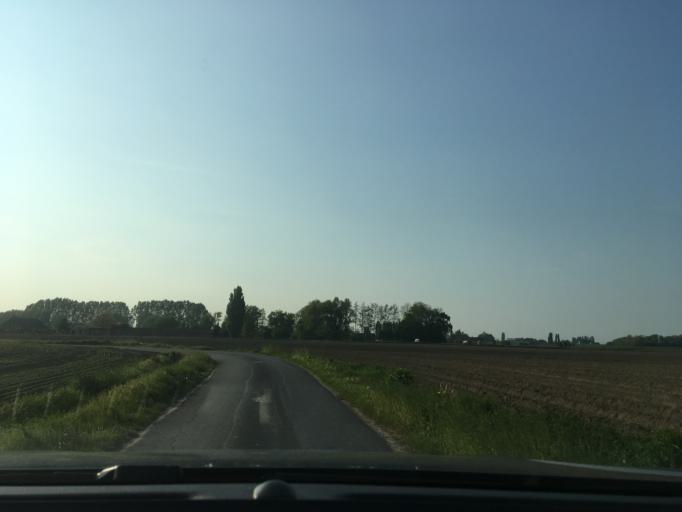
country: BE
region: Flanders
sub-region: Provincie West-Vlaanderen
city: Lichtervelde
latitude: 51.0216
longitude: 3.1617
